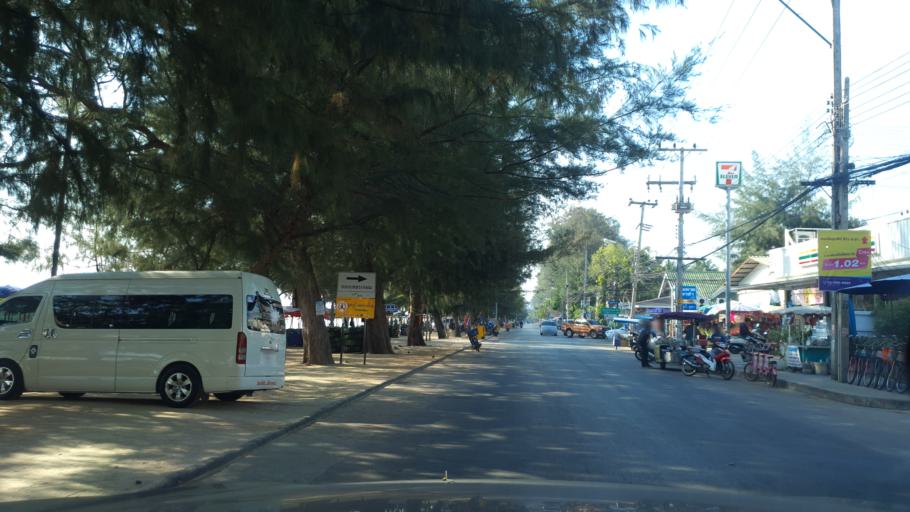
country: TH
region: Phetchaburi
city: Cha-am
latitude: 12.7898
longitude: 99.9821
